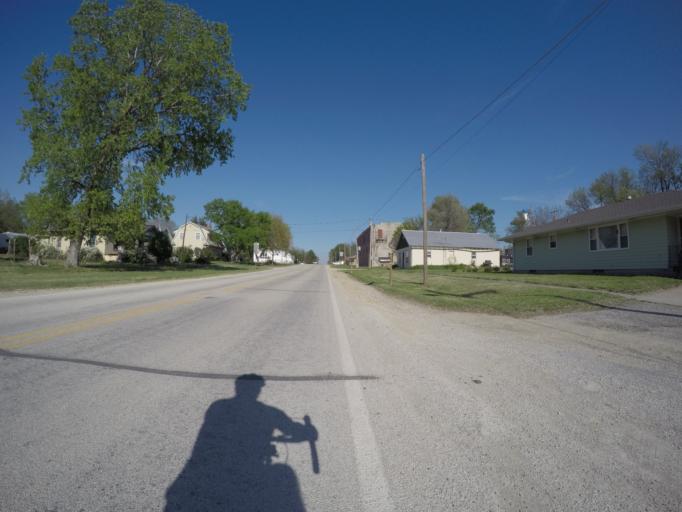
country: US
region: Kansas
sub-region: Riley County
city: Fort Riley North
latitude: 39.2988
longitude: -96.8264
